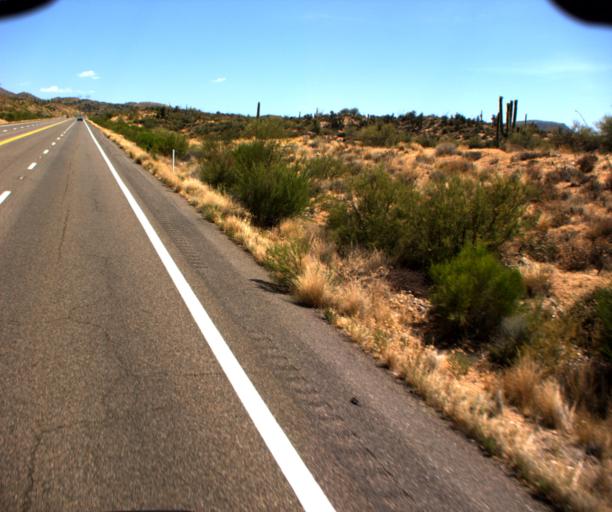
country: US
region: Arizona
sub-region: Gila County
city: Miami
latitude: 33.5762
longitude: -110.9583
